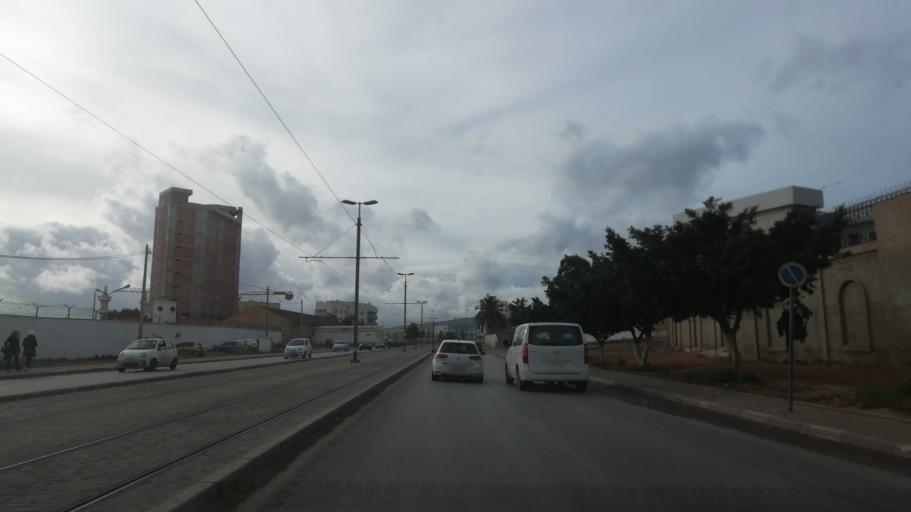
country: DZ
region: Oran
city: Oran
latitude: 35.6968
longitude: -0.6098
